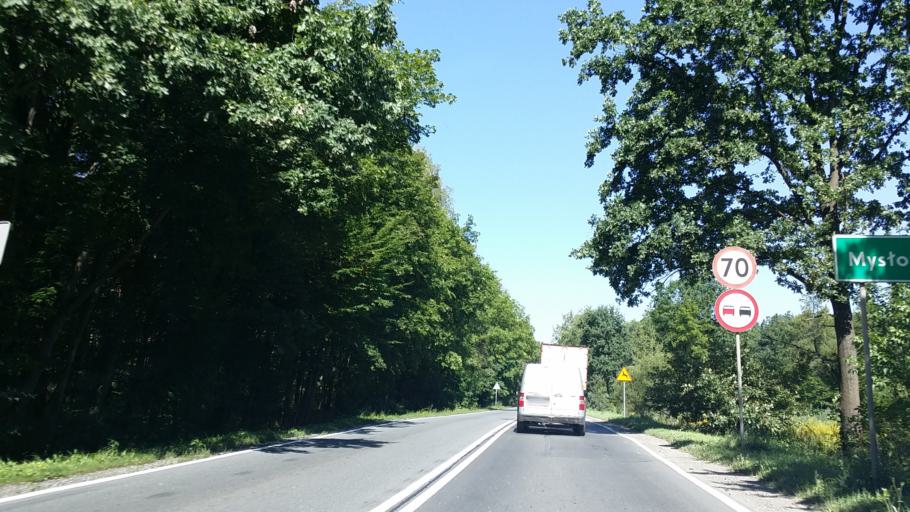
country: PL
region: Silesian Voivodeship
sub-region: Powiat bierunsko-ledzinski
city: Imielin
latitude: 50.1589
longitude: 19.1768
